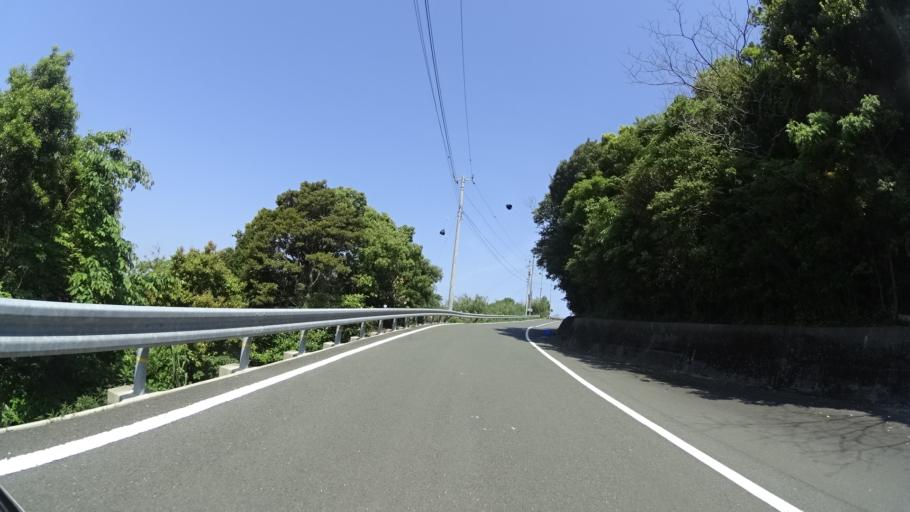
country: JP
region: Oita
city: Tsukumiura
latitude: 33.3585
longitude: 132.0375
